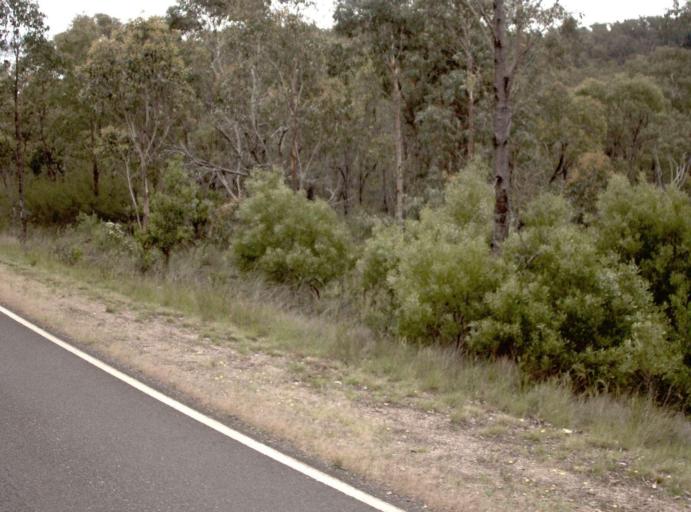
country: AU
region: Victoria
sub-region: East Gippsland
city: Bairnsdale
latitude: -37.6367
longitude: 147.2387
